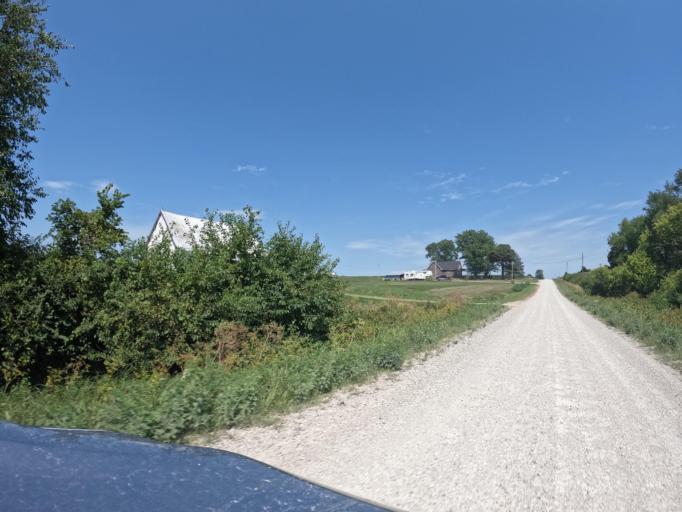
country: US
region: Iowa
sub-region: Henry County
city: Mount Pleasant
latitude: 40.8900
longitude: -91.6509
